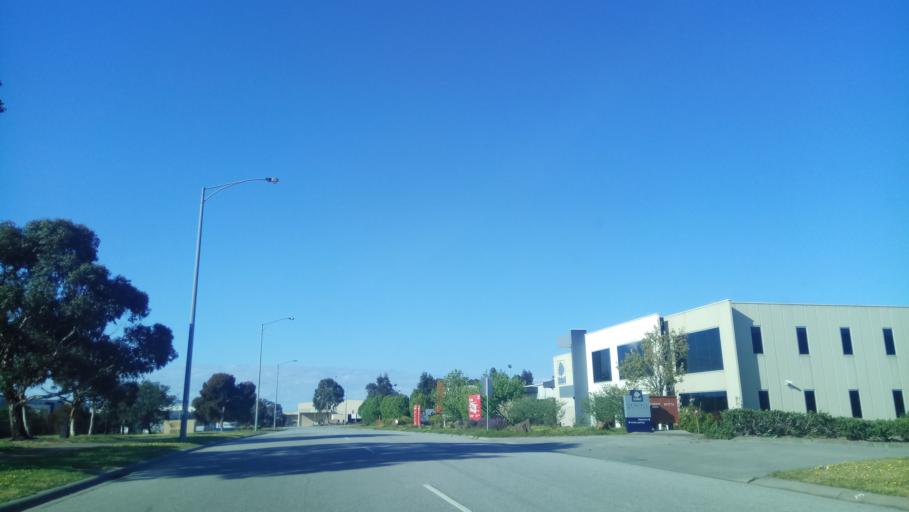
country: AU
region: Victoria
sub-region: Monash
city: Oakleigh South
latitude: -37.9457
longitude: 145.0841
